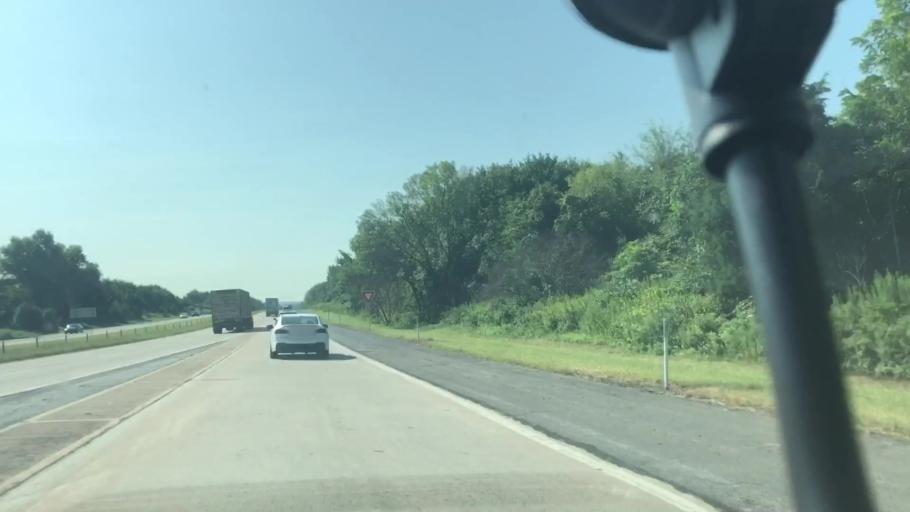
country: US
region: Pennsylvania
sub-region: Montgomery County
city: Limerick
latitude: 40.2144
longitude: -75.5430
